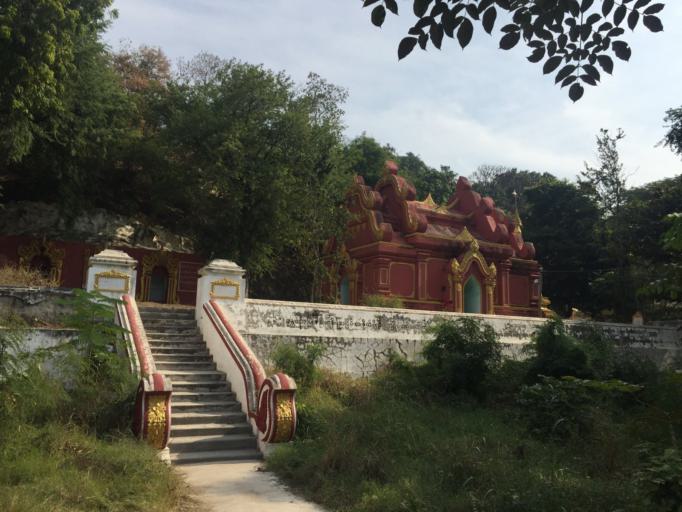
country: MM
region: Sagain
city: Sagaing
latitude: 21.9010
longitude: 95.9964
